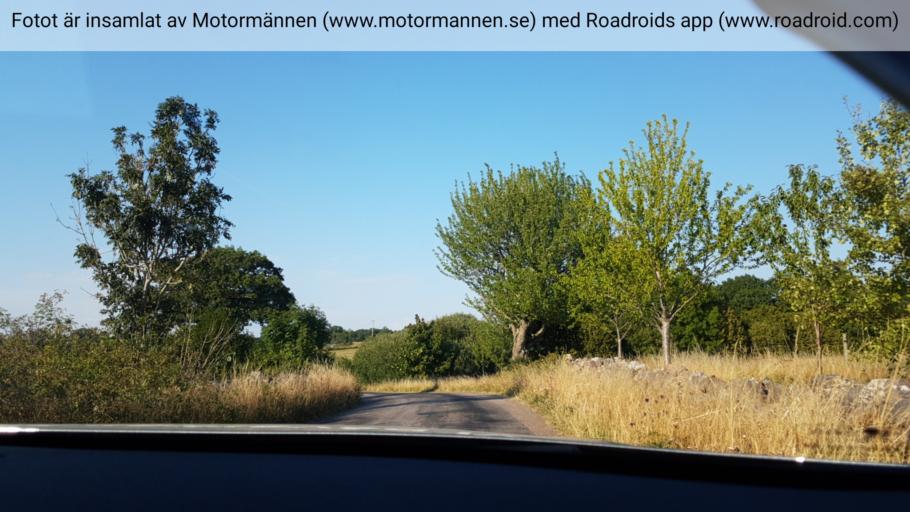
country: SE
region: Vaestra Goetaland
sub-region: Skovde Kommun
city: Stopen
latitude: 58.4935
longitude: 13.7716
